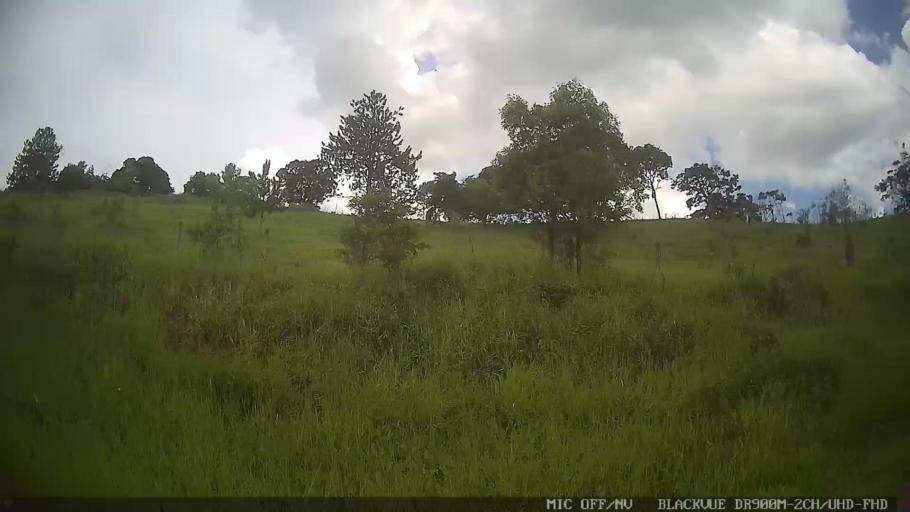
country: BR
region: Minas Gerais
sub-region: Extrema
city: Extrema
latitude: -22.8483
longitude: -46.2662
